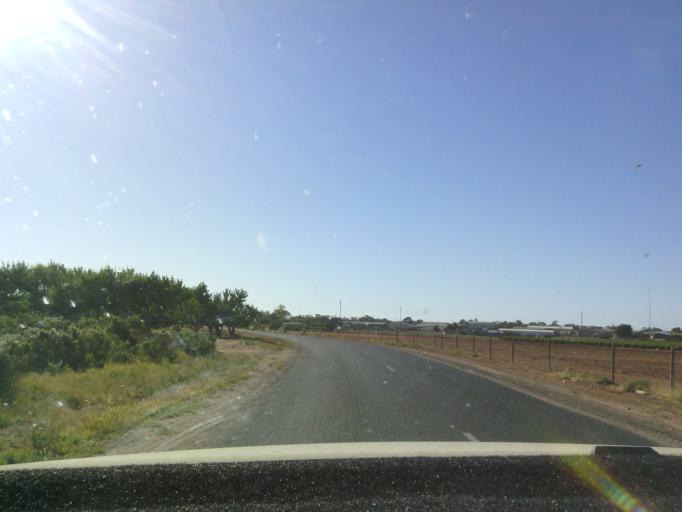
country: AU
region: South Australia
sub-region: Berri and Barmera
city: Berri
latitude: -34.2653
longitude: 140.5980
